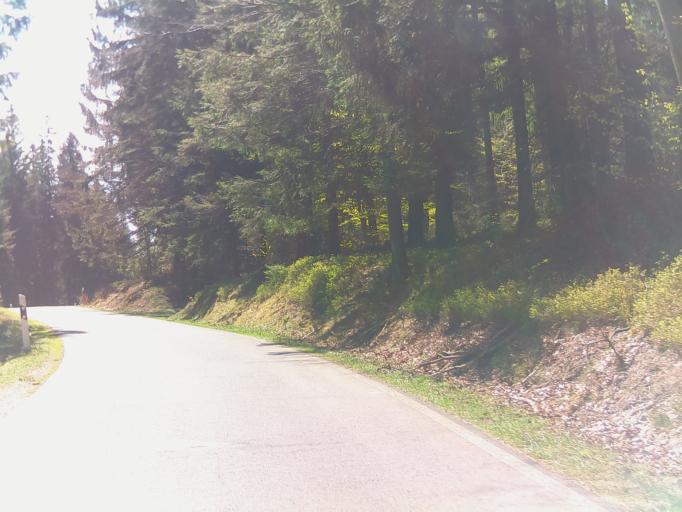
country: DE
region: Thuringia
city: Frauenwald
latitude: 50.5371
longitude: 10.8572
